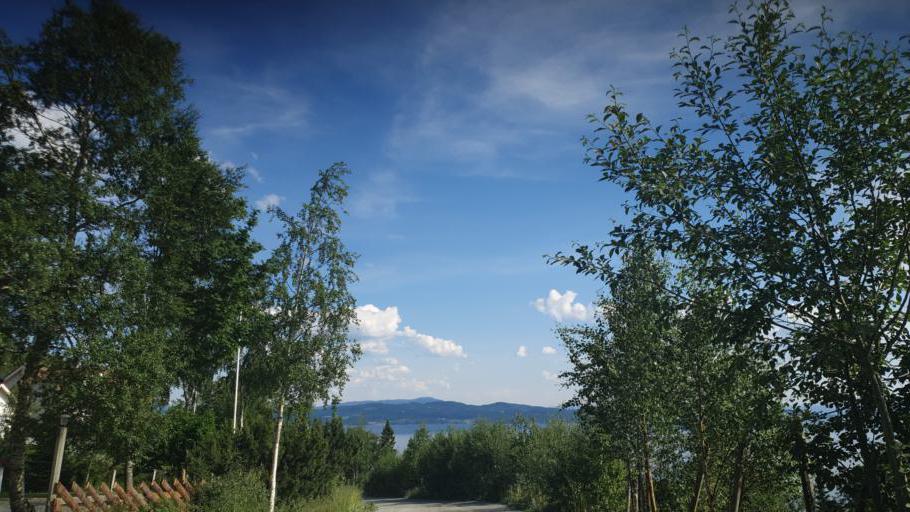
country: NO
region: Nord-Trondelag
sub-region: Leksvik
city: Leksvik
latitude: 63.6785
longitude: 10.6559
